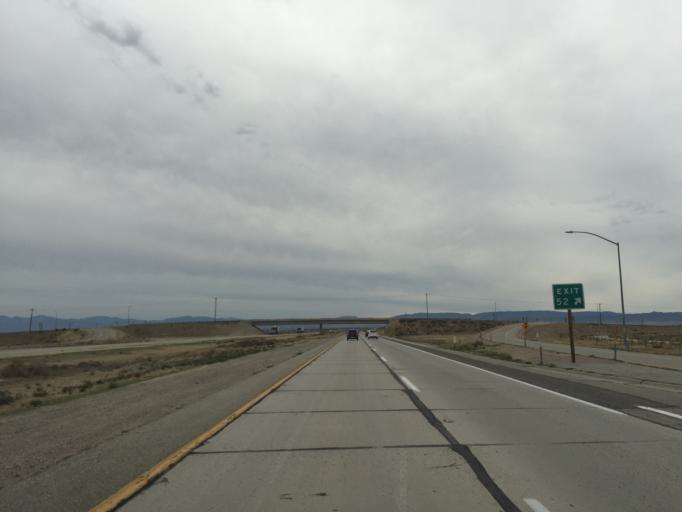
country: US
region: California
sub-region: Kern County
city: Rosamond
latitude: 34.8233
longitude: -118.1705
